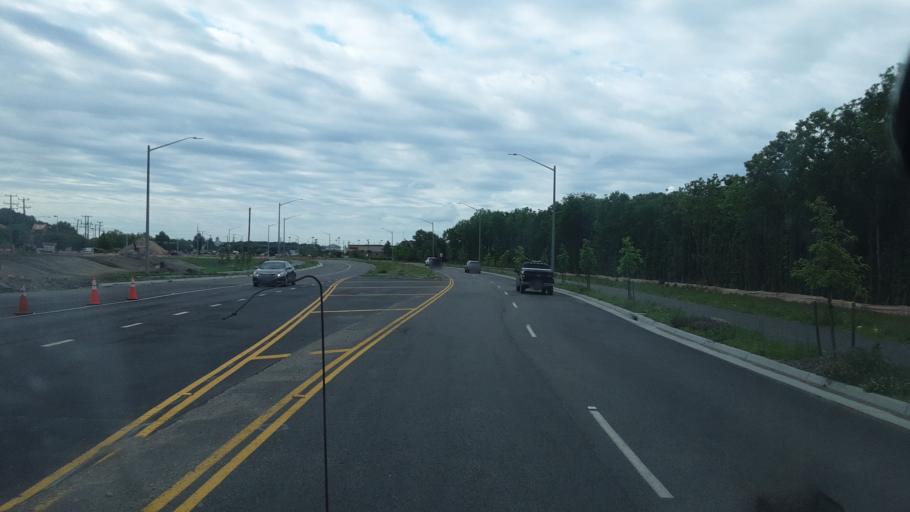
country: US
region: Virginia
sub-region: City of Virginia Beach
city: Virginia Beach
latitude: 36.7557
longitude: -76.0118
